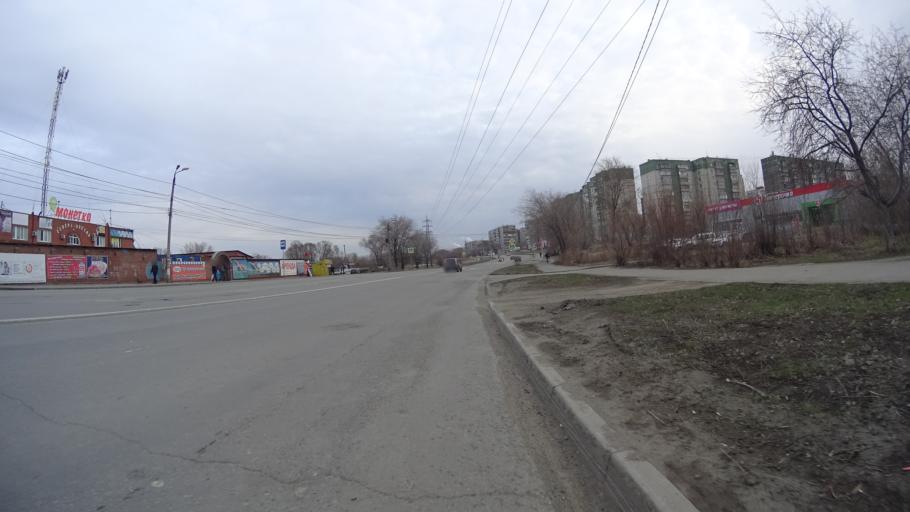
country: RU
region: Chelyabinsk
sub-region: Gorod Chelyabinsk
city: Chelyabinsk
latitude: 55.1877
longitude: 61.4843
